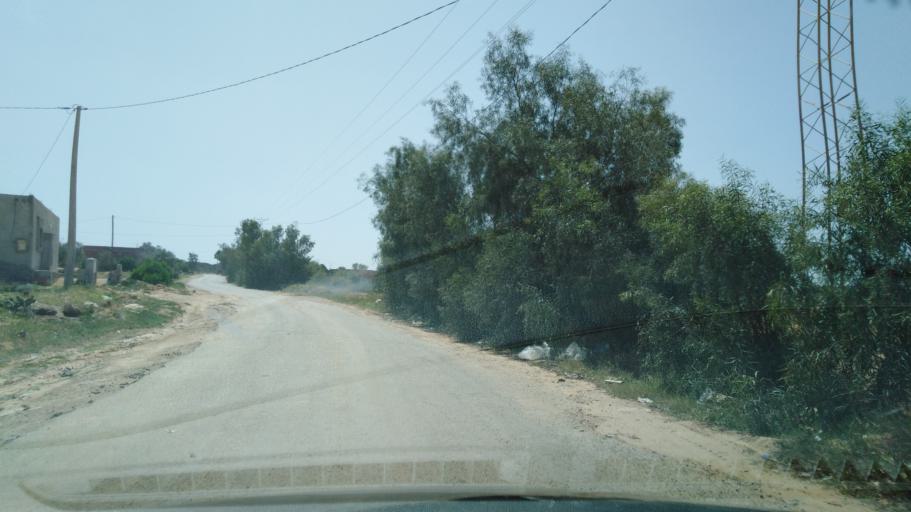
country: TN
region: Safaqis
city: Sfax
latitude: 34.7217
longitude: 10.5305
